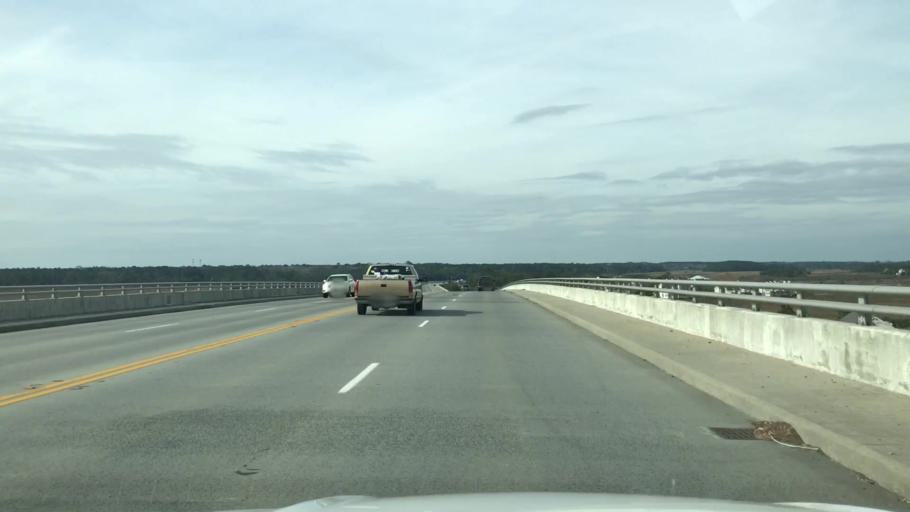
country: US
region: South Carolina
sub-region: Charleston County
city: Charleston
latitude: 32.7526
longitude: -80.0110
